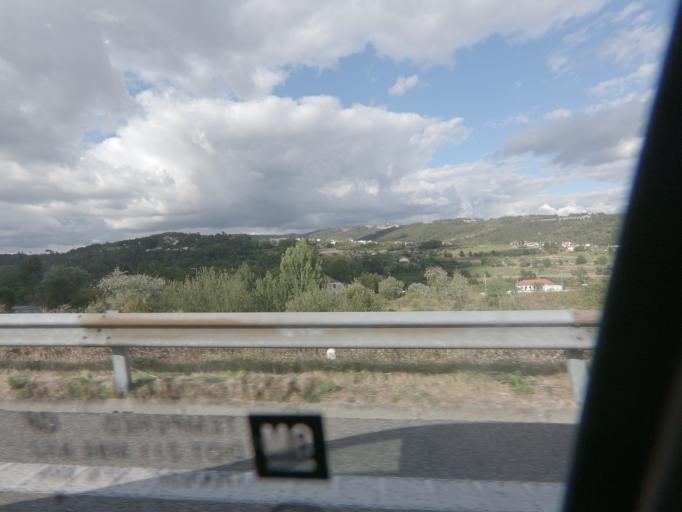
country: PT
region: Porto
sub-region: Marco de Canaveses
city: Marco de Canavezes
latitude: 41.2313
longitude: -8.1766
